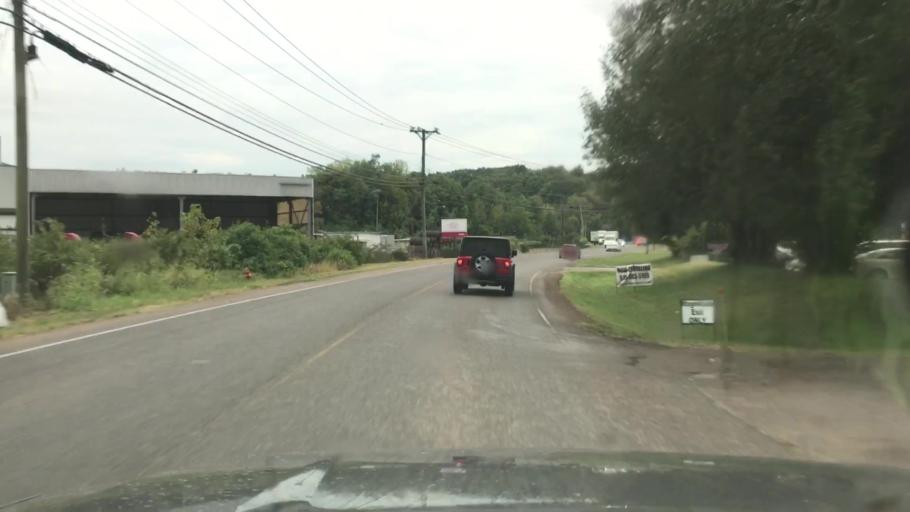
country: US
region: Tennessee
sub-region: Davidson County
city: Lakewood
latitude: 36.1839
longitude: -86.6244
